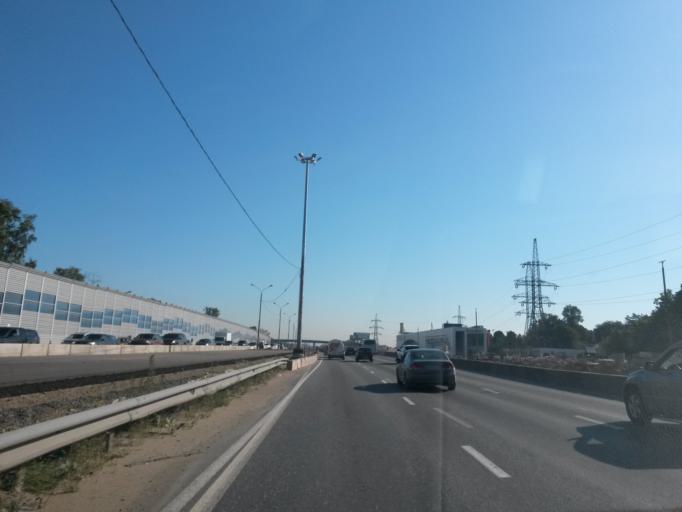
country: RU
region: Moskovskaya
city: Druzhba
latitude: 55.8897
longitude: 37.7405
